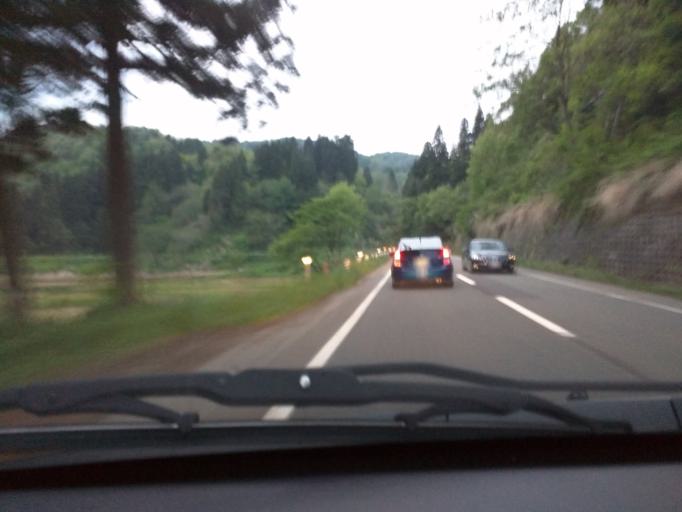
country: JP
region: Niigata
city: Ojiya
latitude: 37.3222
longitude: 138.6848
